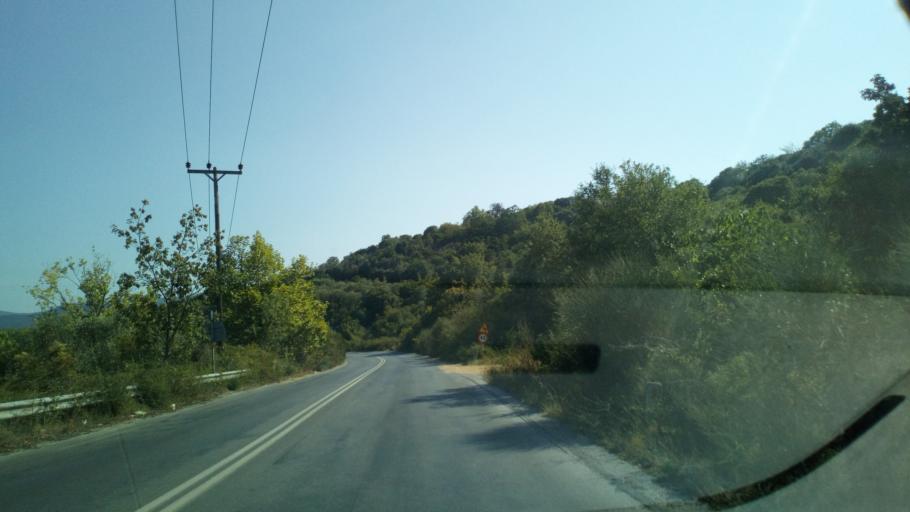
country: GR
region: Central Macedonia
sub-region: Nomos Thessalonikis
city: Stavros
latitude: 40.6140
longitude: 23.7774
